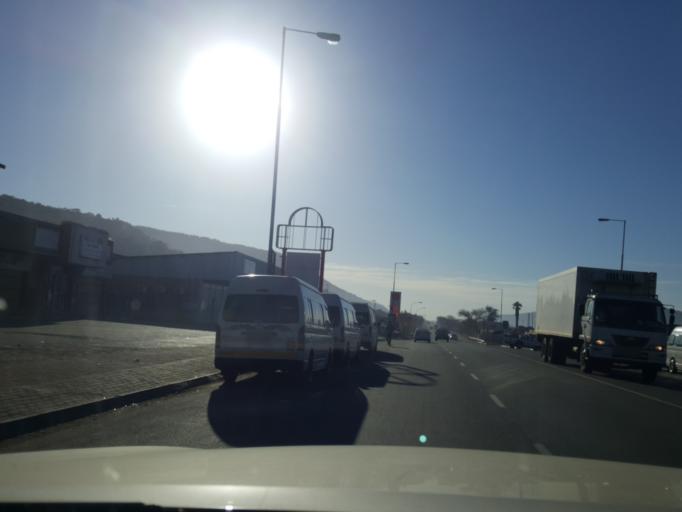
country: ZA
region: North-West
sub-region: Ngaka Modiri Molema District Municipality
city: Zeerust
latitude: -25.5438
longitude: 26.0847
